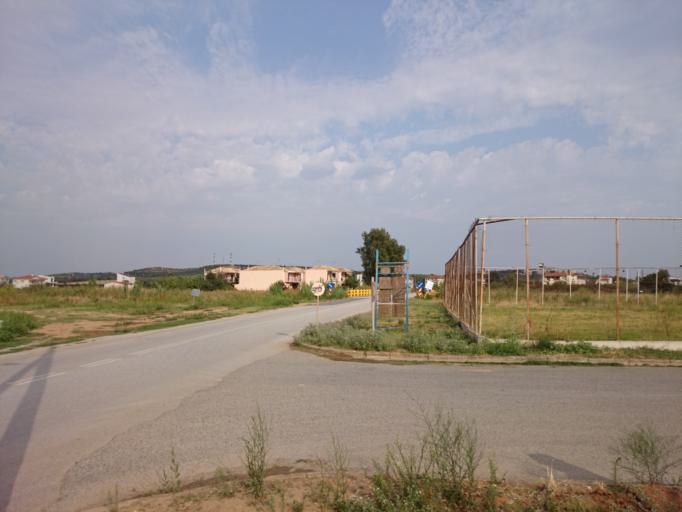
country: GR
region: Central Macedonia
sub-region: Nomos Chalkidikis
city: Nea Moudhania
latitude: 40.2510
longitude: 23.2541
